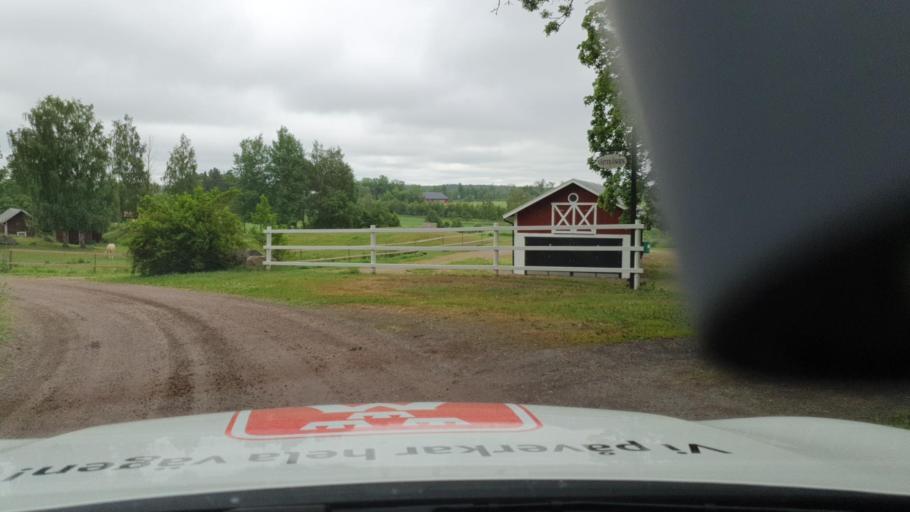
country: SE
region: Vaestra Goetaland
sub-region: Skovde Kommun
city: Stopen
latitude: 58.4004
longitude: 13.9877
